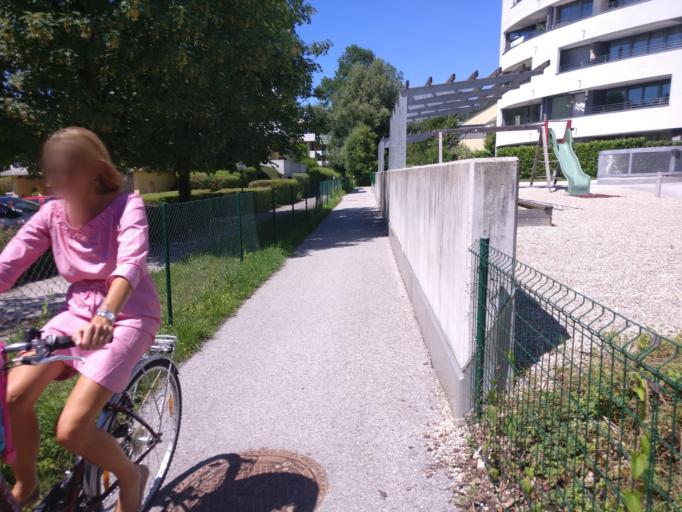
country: AT
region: Salzburg
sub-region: Salzburg Stadt
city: Salzburg
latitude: 47.7870
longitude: 13.0474
